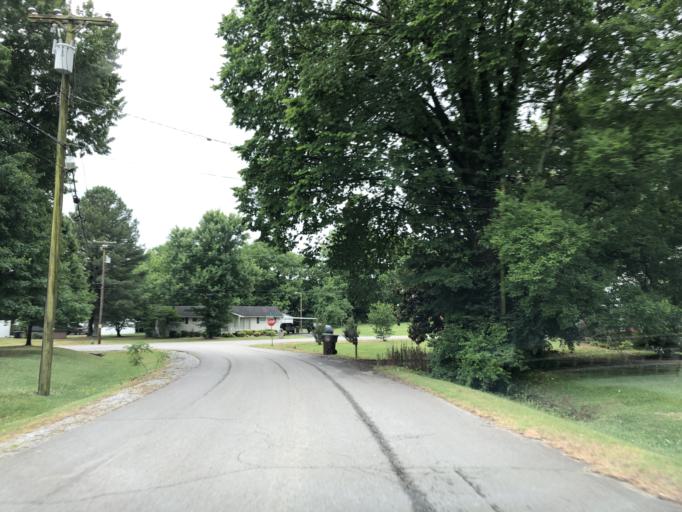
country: US
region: Tennessee
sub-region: Davidson County
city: Goodlettsville
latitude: 36.2713
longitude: -86.7661
